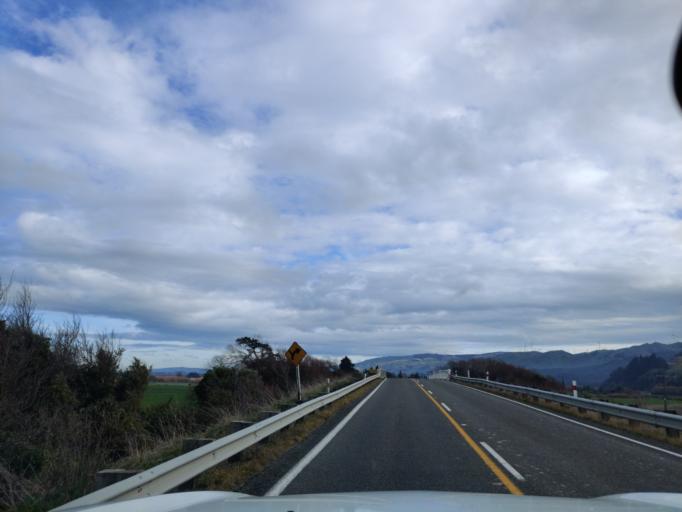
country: NZ
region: Manawatu-Wanganui
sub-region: Palmerston North City
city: Palmerston North
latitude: -40.3344
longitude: 175.8436
